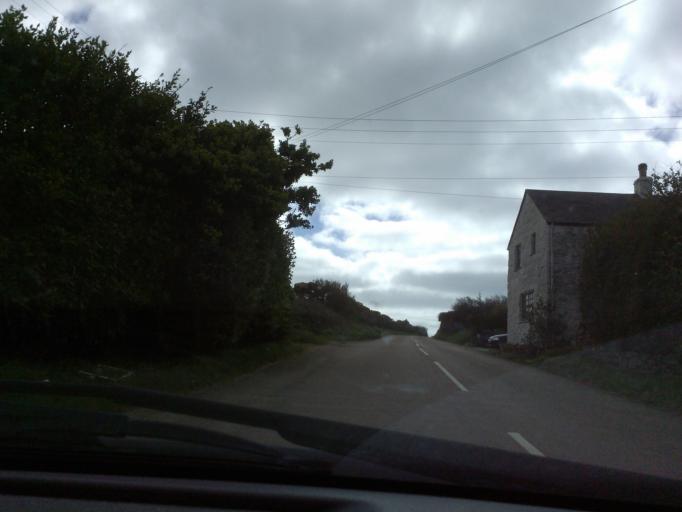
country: GB
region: England
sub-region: Cornwall
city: St. Buryan
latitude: 50.0598
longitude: -5.6363
